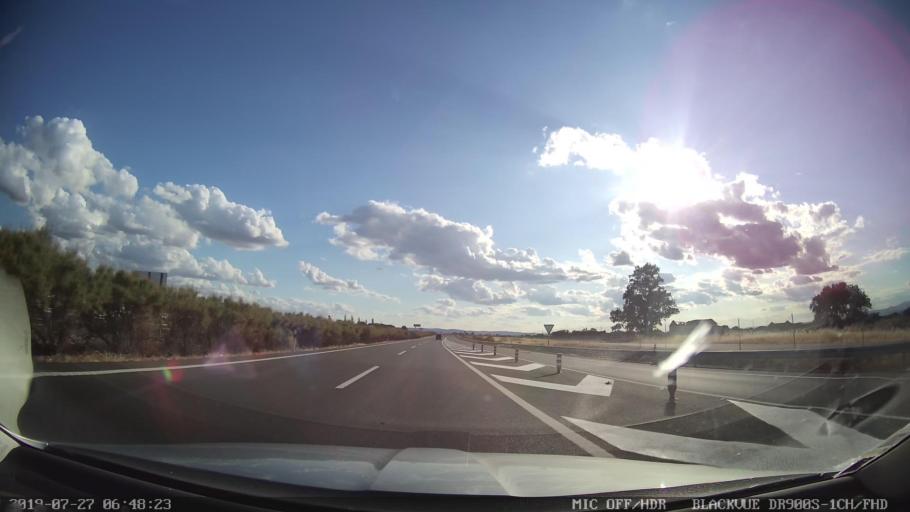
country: ES
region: Extremadura
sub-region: Provincia de Caceres
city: Millanes
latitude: 39.8650
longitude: -5.5991
